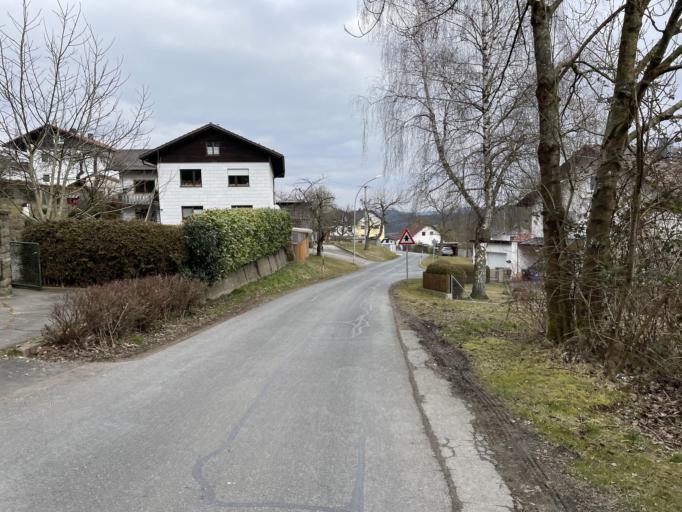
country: DE
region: Bavaria
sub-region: Upper Palatinate
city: Runding
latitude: 49.2168
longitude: 12.7648
